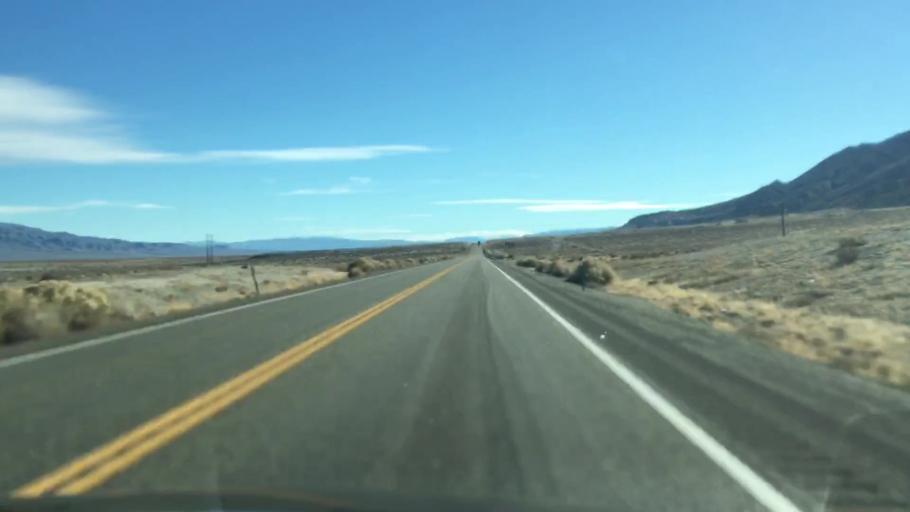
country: US
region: Nevada
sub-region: Mineral County
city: Hawthorne
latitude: 38.8148
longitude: -118.7667
